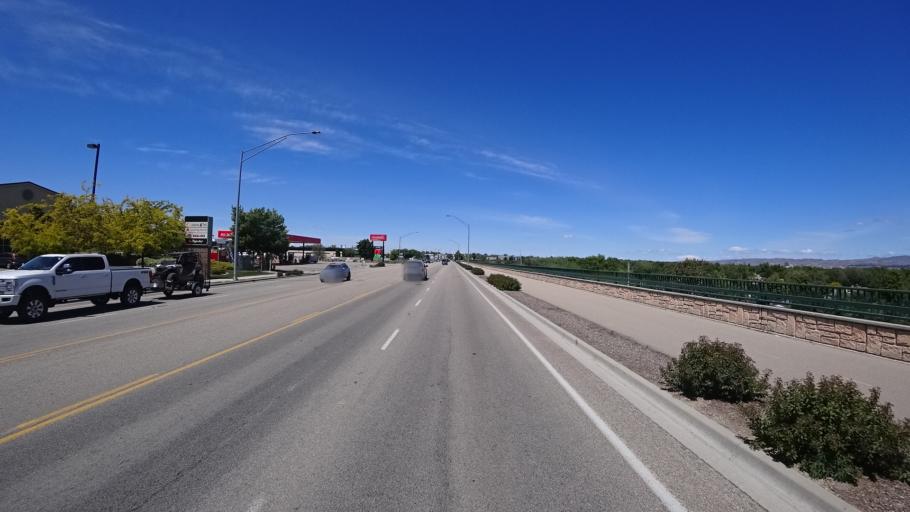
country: US
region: Idaho
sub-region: Ada County
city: Boise
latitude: 43.5717
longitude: -116.1883
